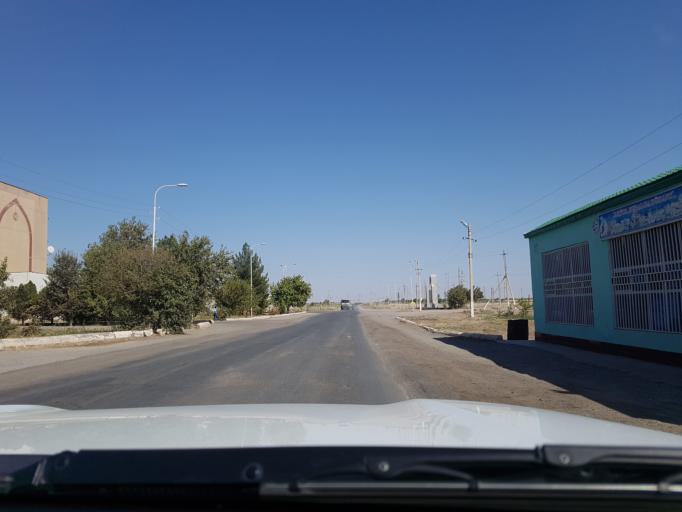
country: IR
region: Razavi Khorasan
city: Sarakhs
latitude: 36.5239
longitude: 61.2266
